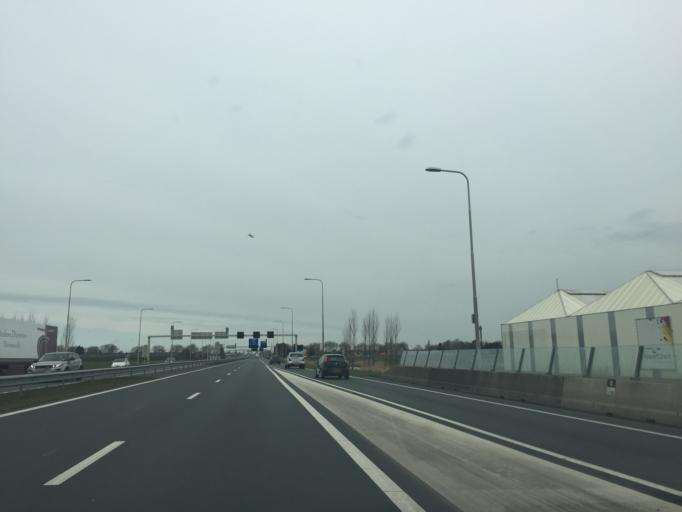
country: NL
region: North Holland
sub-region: Gemeente Aalsmeer
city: Aalsmeer
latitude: 52.2631
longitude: 4.7940
